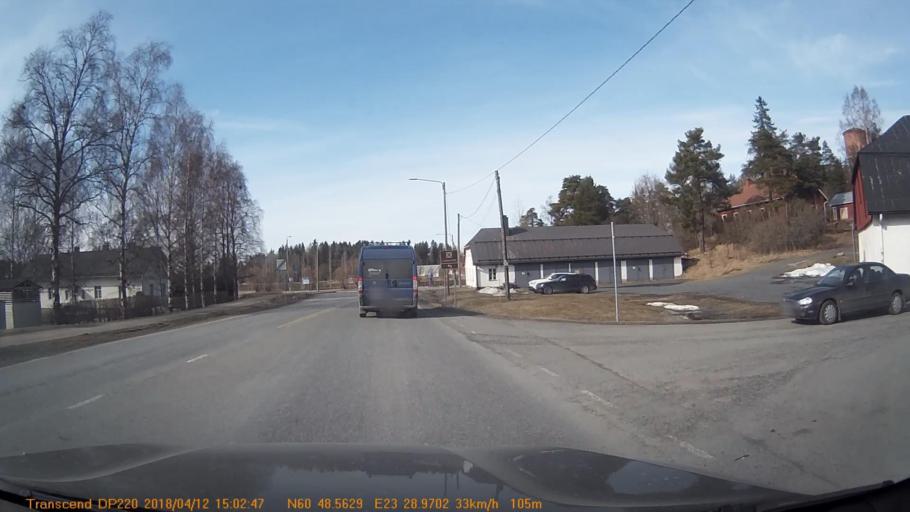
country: FI
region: Haeme
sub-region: Forssa
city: Jokioinen
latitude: 60.8095
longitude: 23.4828
